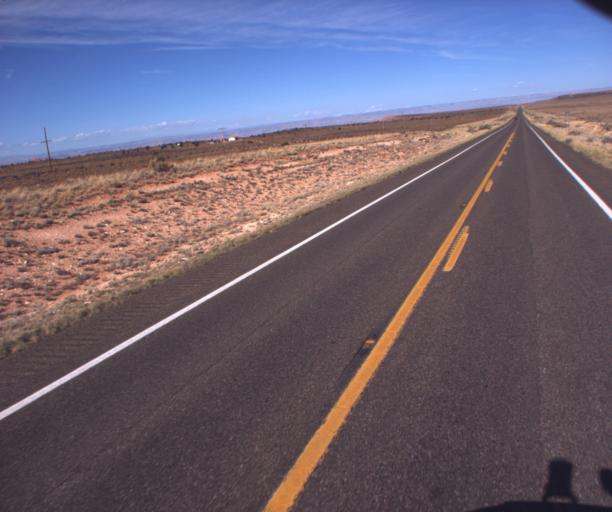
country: US
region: Arizona
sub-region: Coconino County
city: LeChee
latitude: 36.7555
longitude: -111.5715
